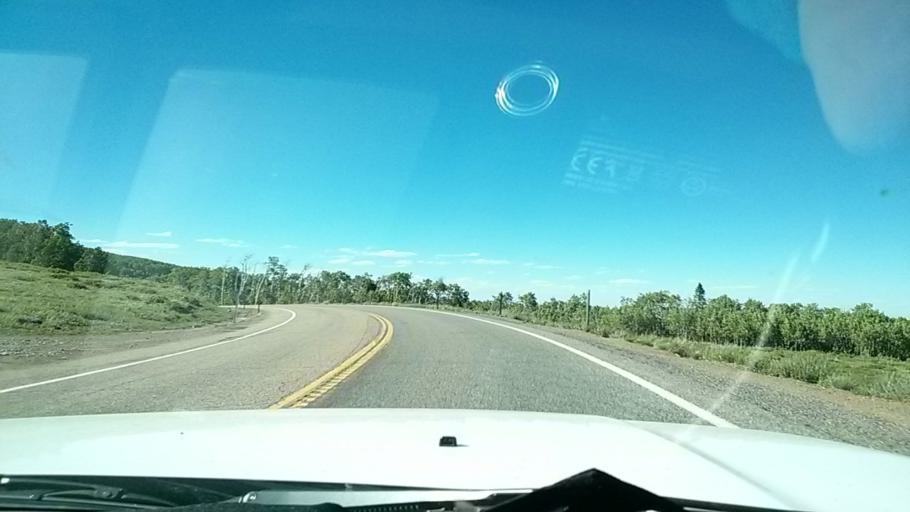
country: US
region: Utah
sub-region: Wayne County
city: Loa
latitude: 38.0436
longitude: -111.3268
